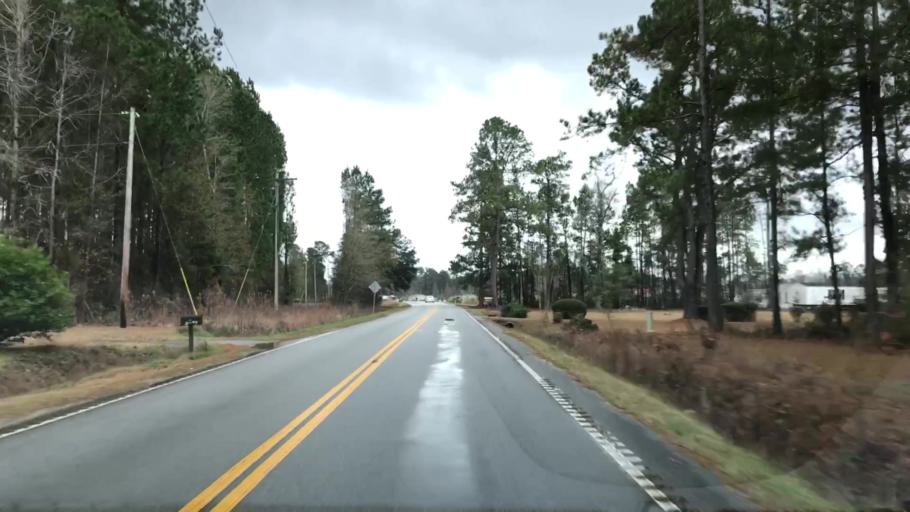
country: US
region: South Carolina
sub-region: Williamsburg County
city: Andrews
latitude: 33.4944
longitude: -79.5078
